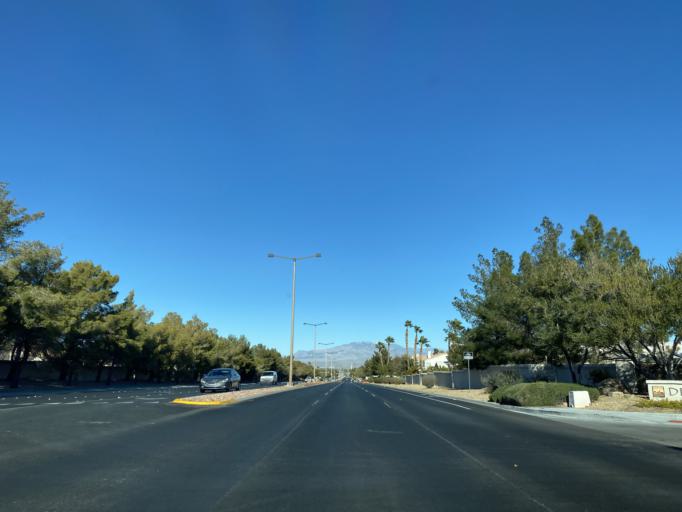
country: US
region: Nevada
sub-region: Clark County
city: Summerlin South
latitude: 36.2061
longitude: -115.2789
